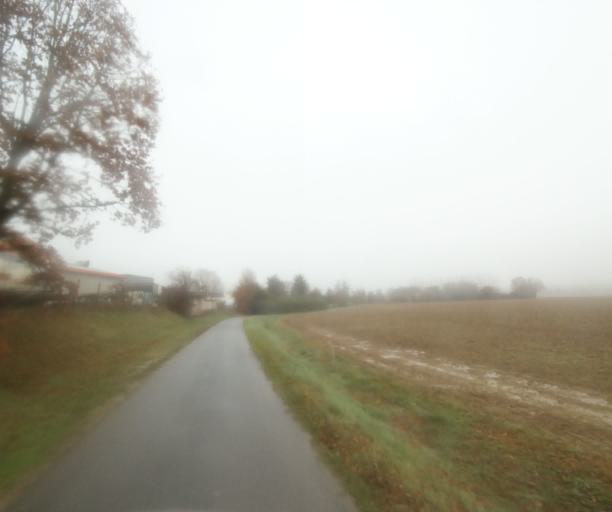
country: FR
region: Midi-Pyrenees
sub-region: Departement de la Haute-Garonne
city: Villemur-sur-Tarn
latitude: 43.8448
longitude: 1.4989
